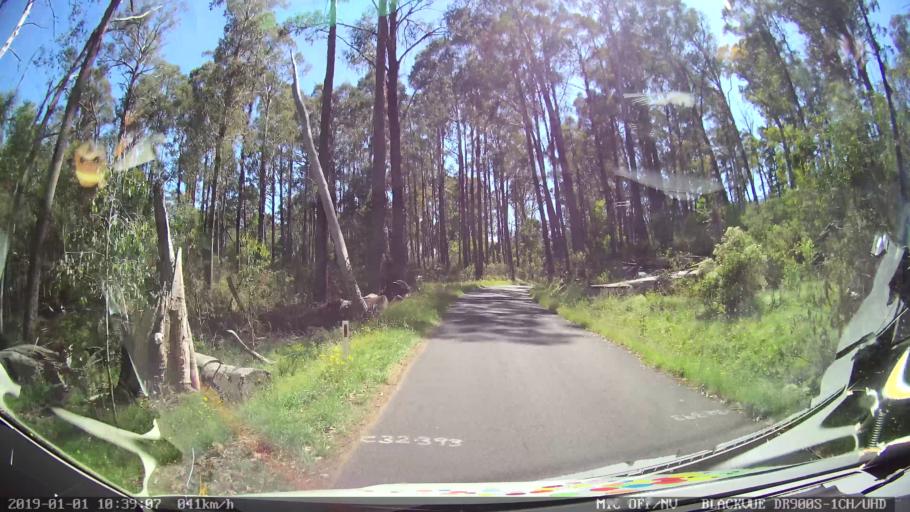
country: AU
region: New South Wales
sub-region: Snowy River
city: Jindabyne
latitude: -36.0414
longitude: 148.3019
